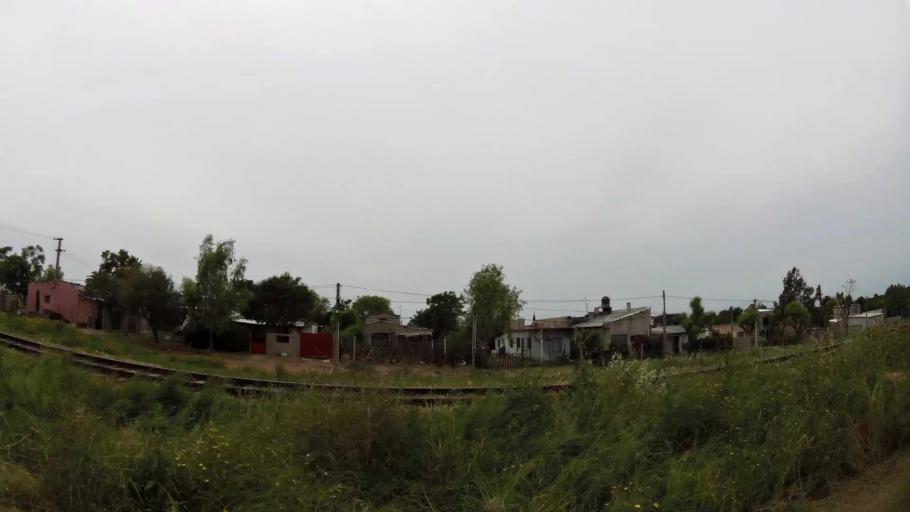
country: UY
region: Canelones
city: La Paz
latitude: -34.7498
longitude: -56.2220
